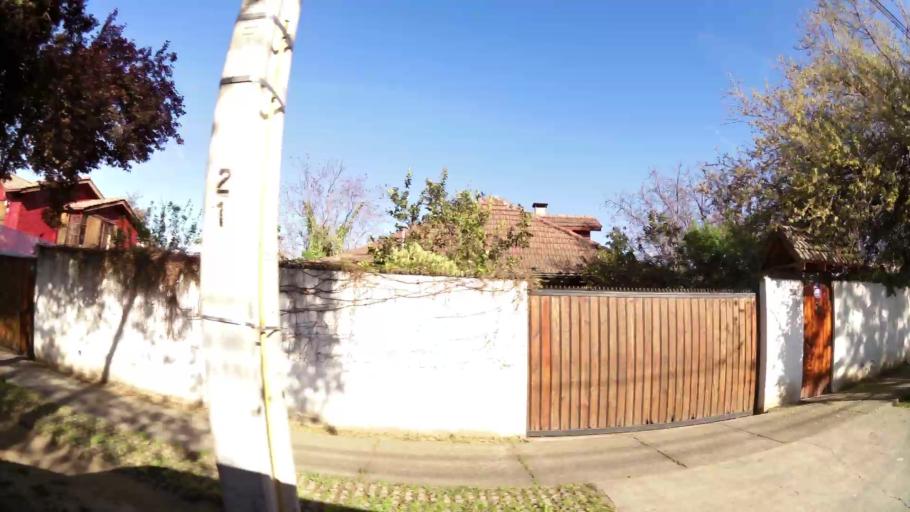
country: CL
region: Santiago Metropolitan
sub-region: Provincia de Santiago
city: Villa Presidente Frei, Nunoa, Santiago, Chile
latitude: -33.4589
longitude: -70.5648
